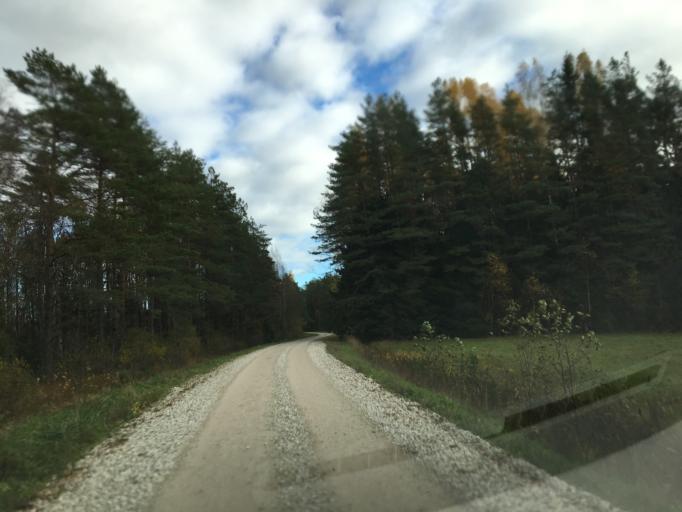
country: EE
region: Tartu
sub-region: Puhja vald
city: Puhja
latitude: 58.4343
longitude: 26.2962
